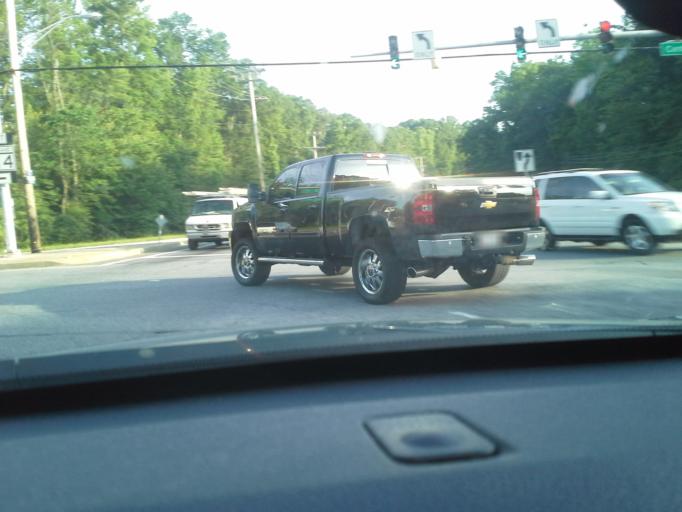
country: US
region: Maryland
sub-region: Anne Arundel County
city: Londontowne
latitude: 38.9268
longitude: -76.5684
